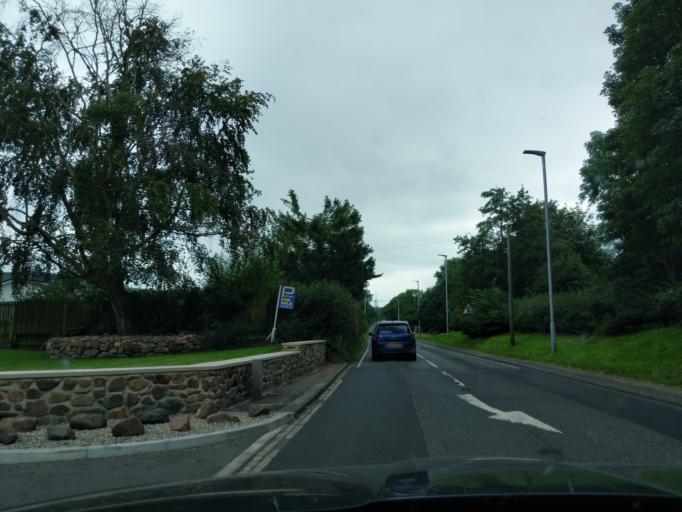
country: GB
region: England
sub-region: Northumberland
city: Wooler
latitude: 55.5435
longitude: -2.0091
